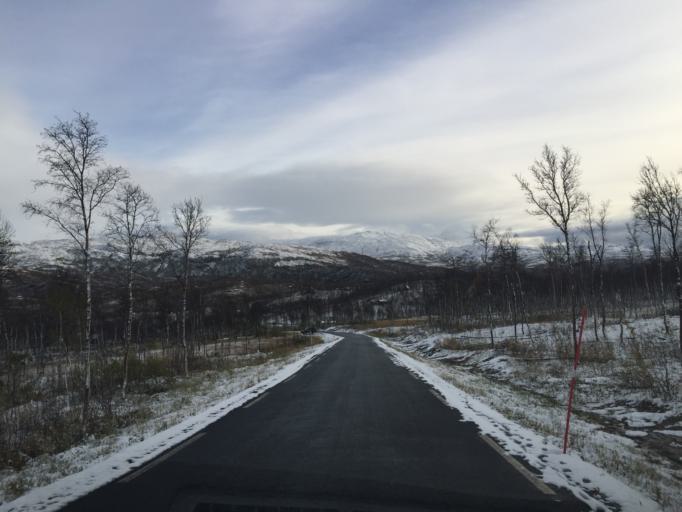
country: NO
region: Nordland
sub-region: Sorfold
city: Straumen
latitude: 67.0865
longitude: 16.0221
